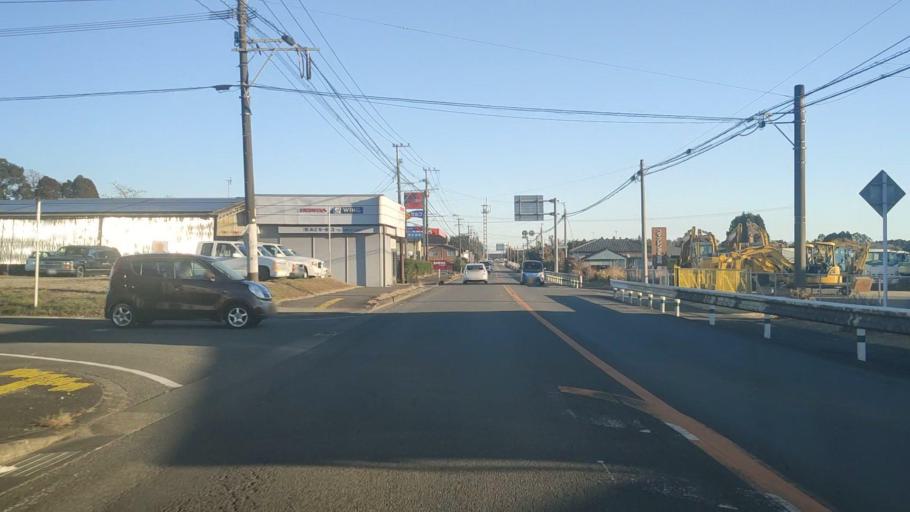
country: JP
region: Miyazaki
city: Takanabe
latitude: 32.1742
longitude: 131.5197
